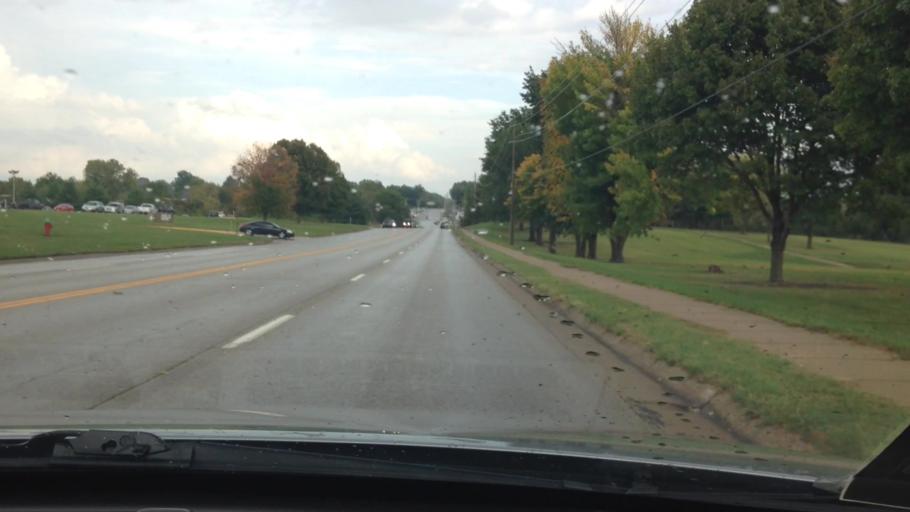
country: US
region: Kansas
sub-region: Leavenworth County
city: Lansing
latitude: 39.2668
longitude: -94.9066
